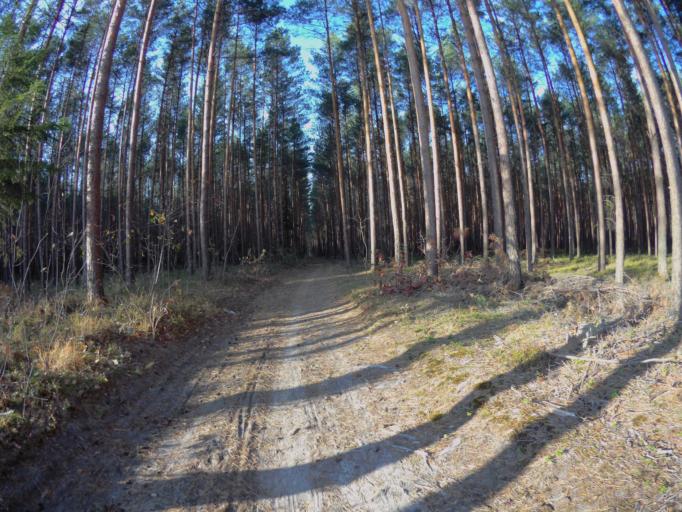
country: PL
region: Subcarpathian Voivodeship
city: Nowa Sarzyna
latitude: 50.3110
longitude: 22.3554
